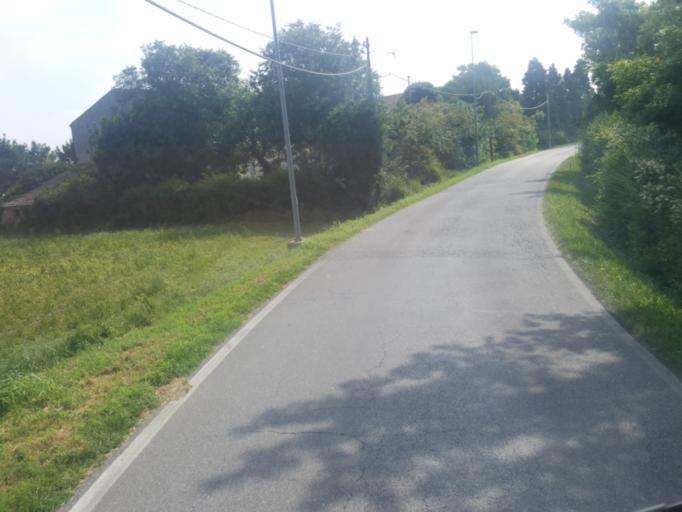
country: IT
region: Veneto
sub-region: Provincia di Rovigo
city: Canaro
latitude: 44.9369
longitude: 11.6682
